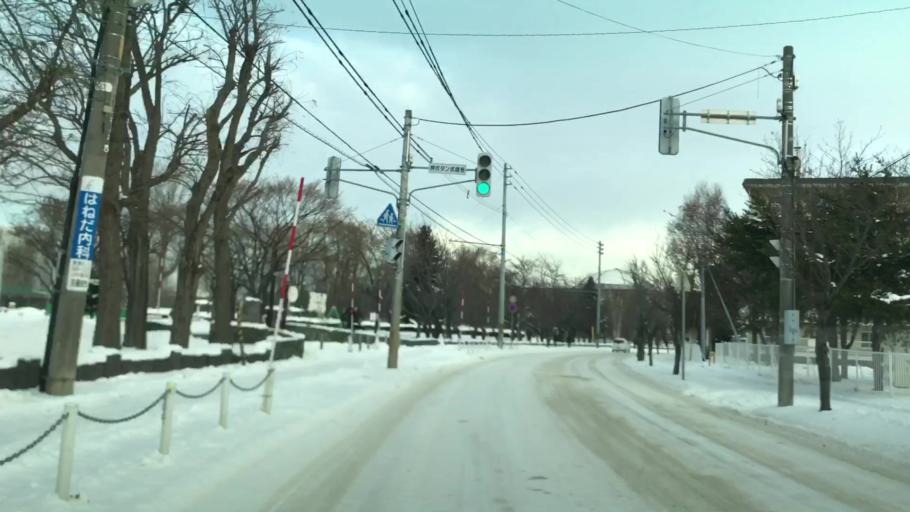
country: JP
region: Hokkaido
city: Sapporo
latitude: 43.0885
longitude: 141.3042
